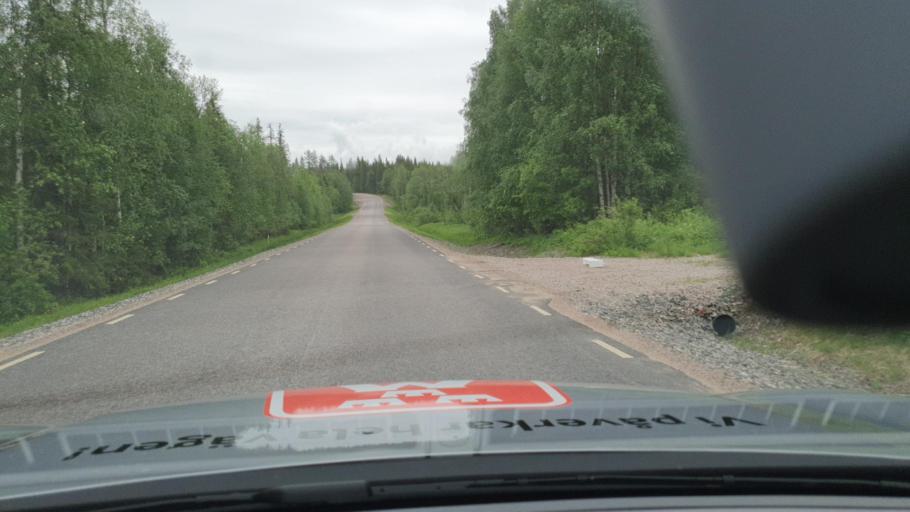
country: SE
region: Norrbotten
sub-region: Overtornea Kommun
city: OEvertornea
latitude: 66.4995
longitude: 23.4260
